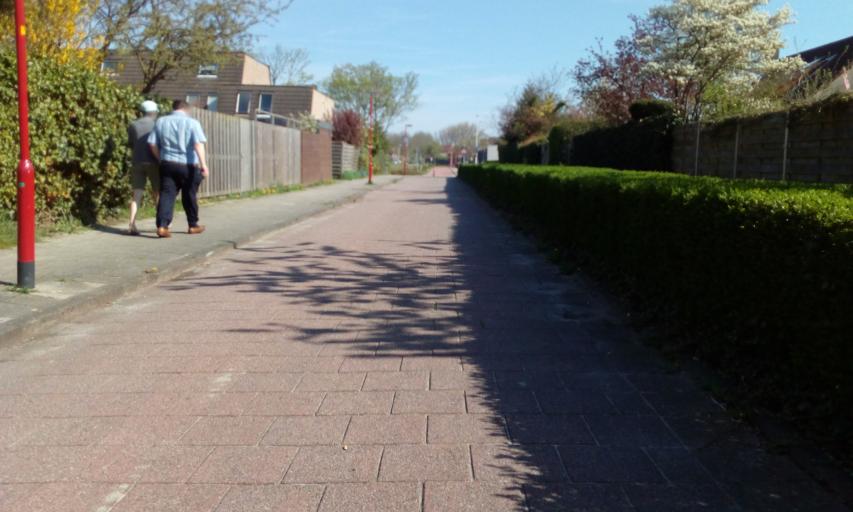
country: NL
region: South Holland
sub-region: Gemeente Zoetermeer
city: Zoetermeer
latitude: 52.0749
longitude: 4.4962
